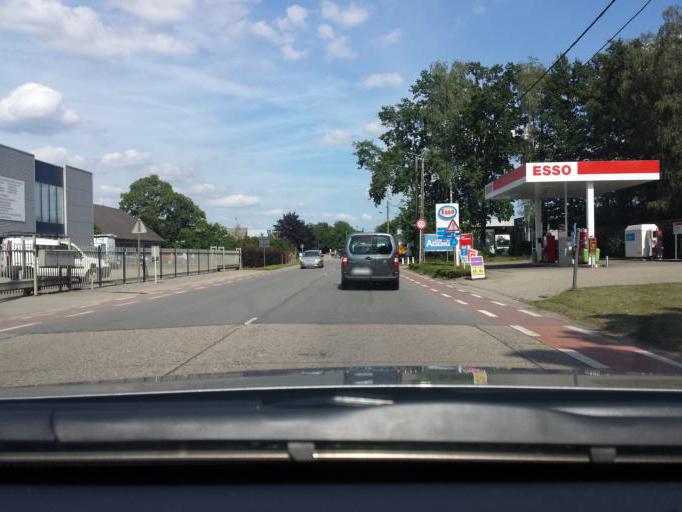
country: BE
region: Flanders
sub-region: Provincie Limburg
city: Lummen
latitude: 50.9956
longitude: 5.2354
